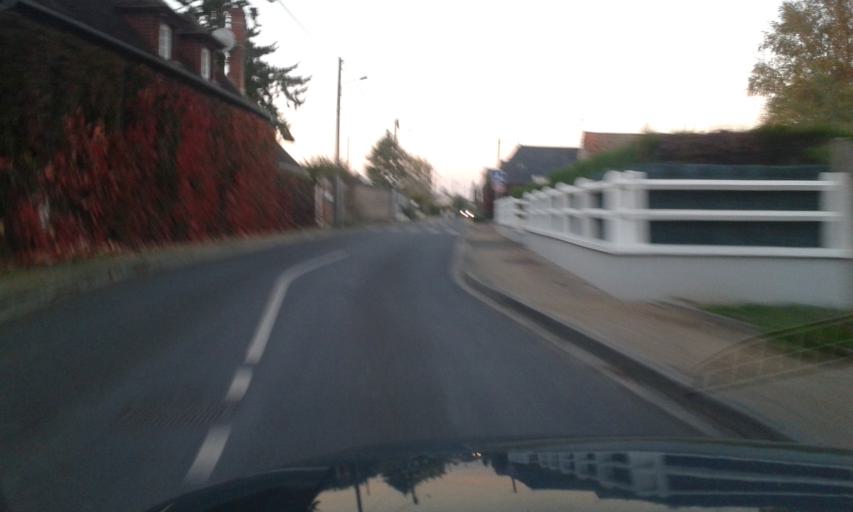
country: FR
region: Centre
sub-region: Departement du Loiret
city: Olivet
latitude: 47.8572
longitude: 1.8811
